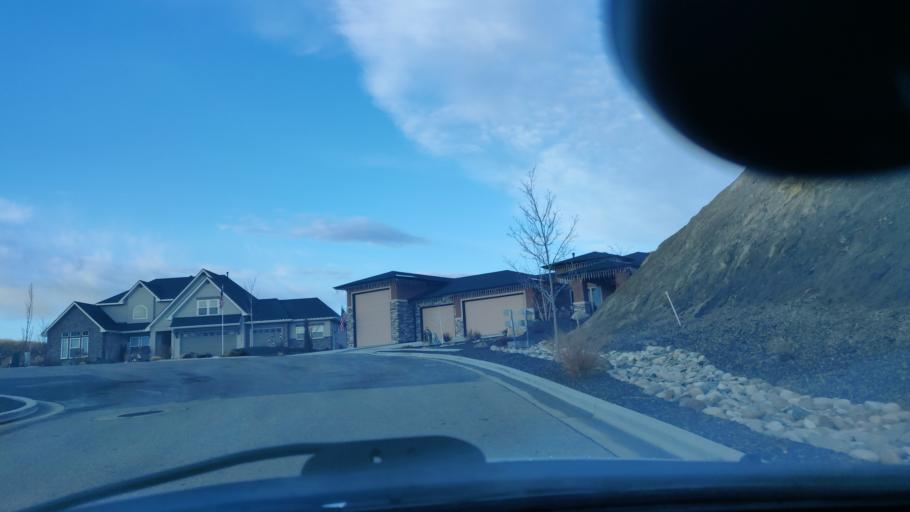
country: US
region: Idaho
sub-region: Ada County
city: Eagle
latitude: 43.7747
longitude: -116.2511
